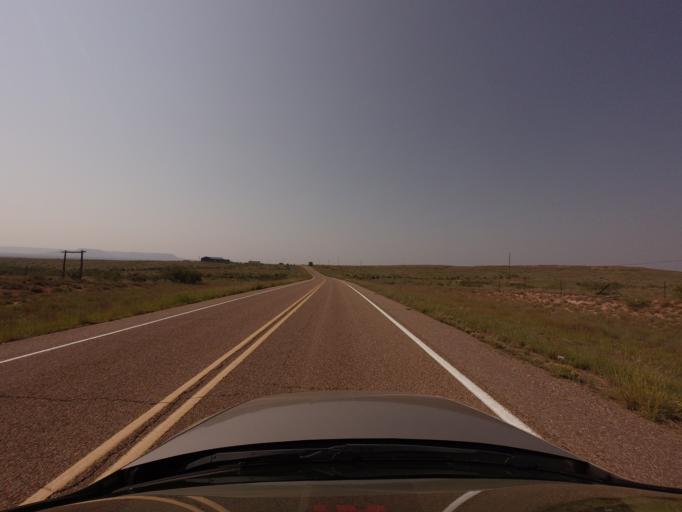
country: US
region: New Mexico
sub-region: Quay County
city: Tucumcari
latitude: 35.1005
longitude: -103.7365
